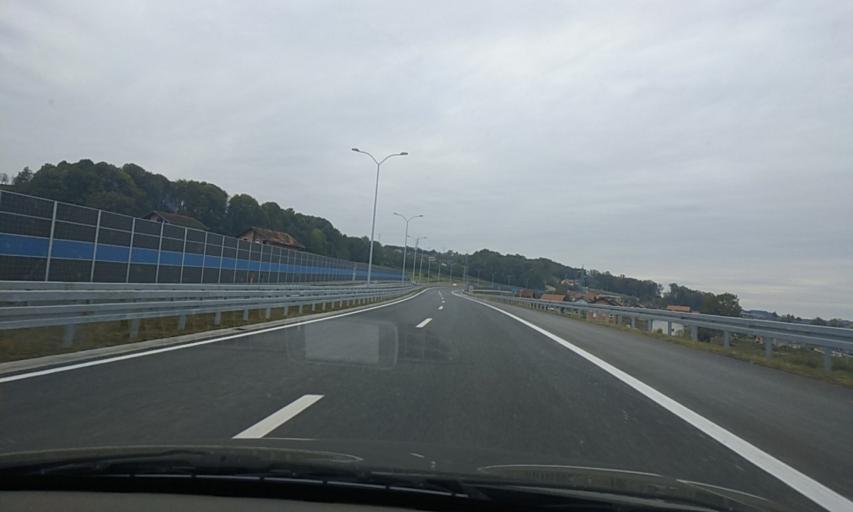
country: BA
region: Republika Srpska
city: Prnjavor
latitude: 44.8634
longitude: 17.6481
